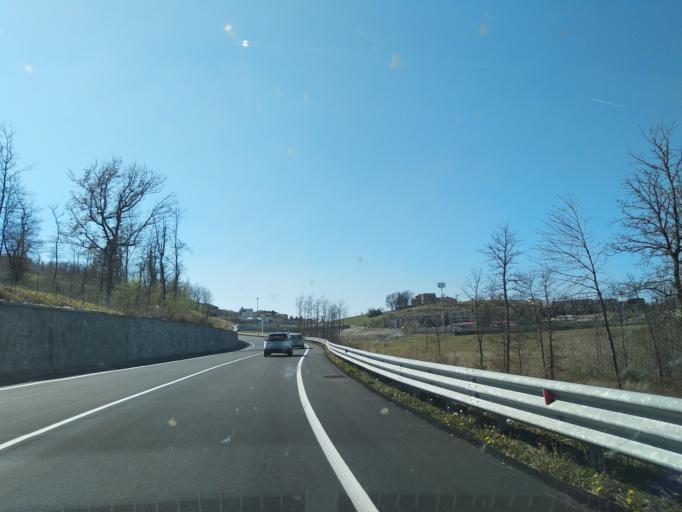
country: IT
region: Emilia-Romagna
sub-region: Provincia di Reggio Emilia
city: Castelnovo ne'Monti
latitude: 44.4344
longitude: 10.4199
